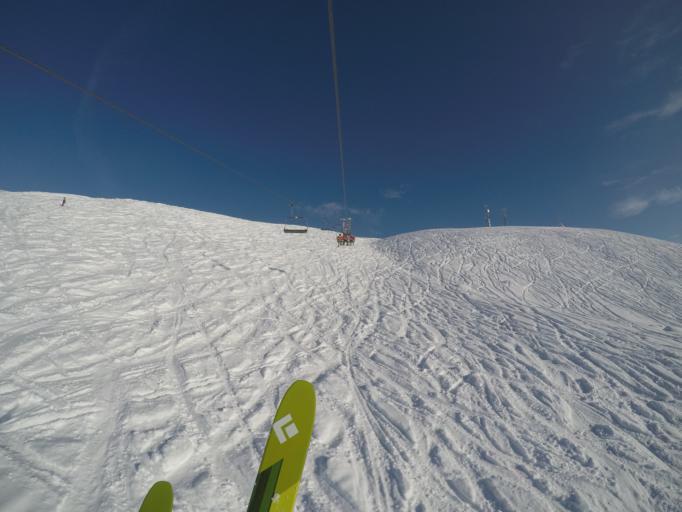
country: GE
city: Gudauri
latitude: 42.4869
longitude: 44.4973
